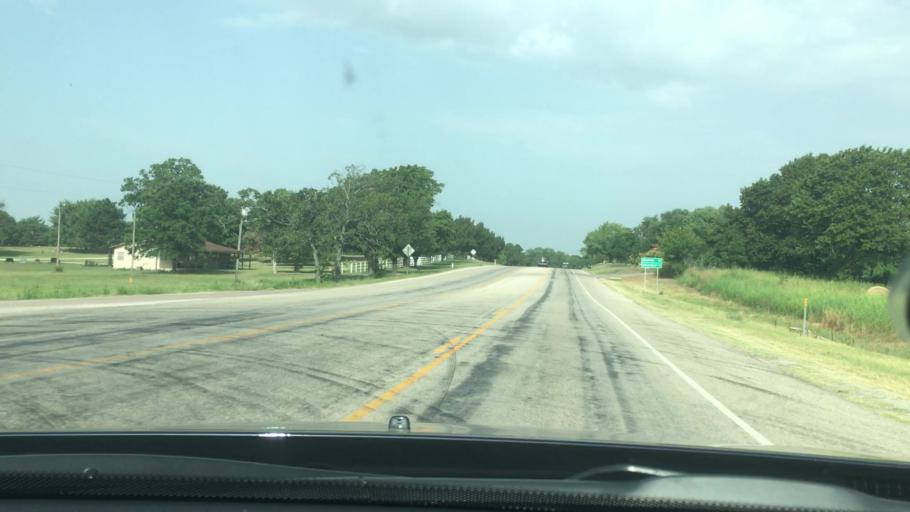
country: US
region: Oklahoma
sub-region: Pontotoc County
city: Ada
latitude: 34.7857
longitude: -96.7297
